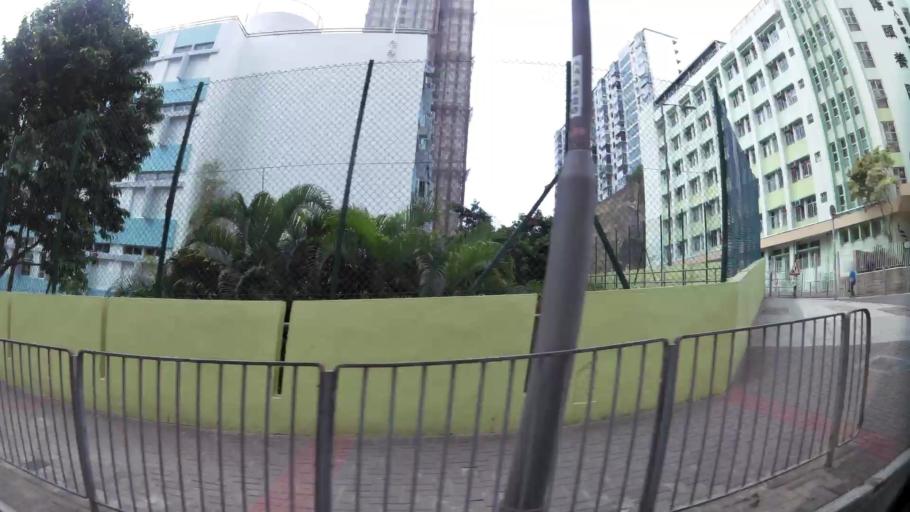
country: HK
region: Kowloon City
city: Kowloon
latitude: 22.3186
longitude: 114.2219
